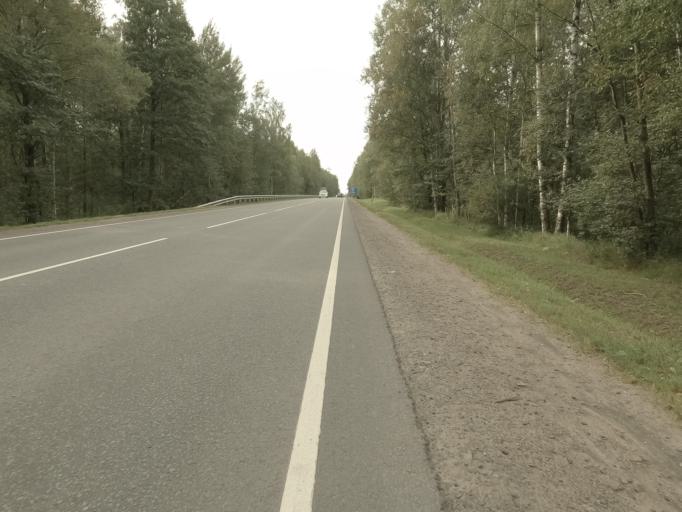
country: RU
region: Leningrad
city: Kirovsk
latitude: 59.8467
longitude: 31.0383
